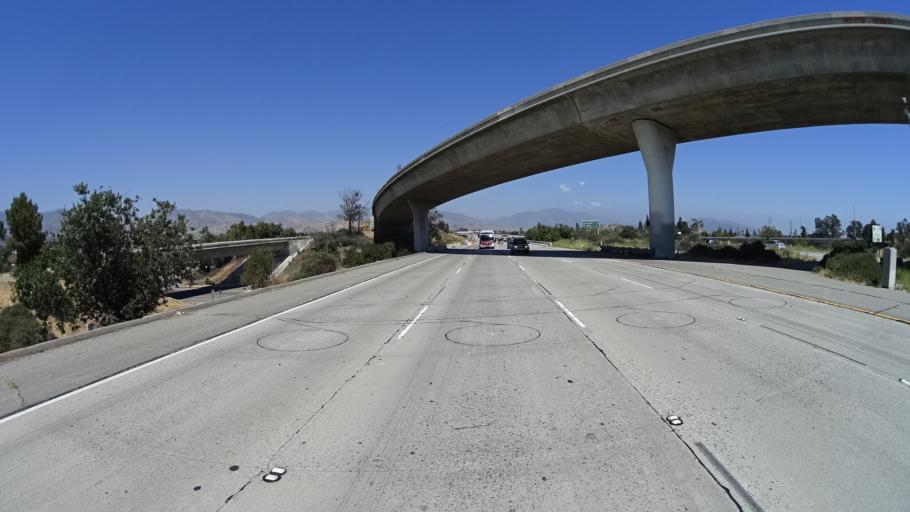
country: US
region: California
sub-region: Los Angeles County
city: San Fernando
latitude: 34.2672
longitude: -118.4422
